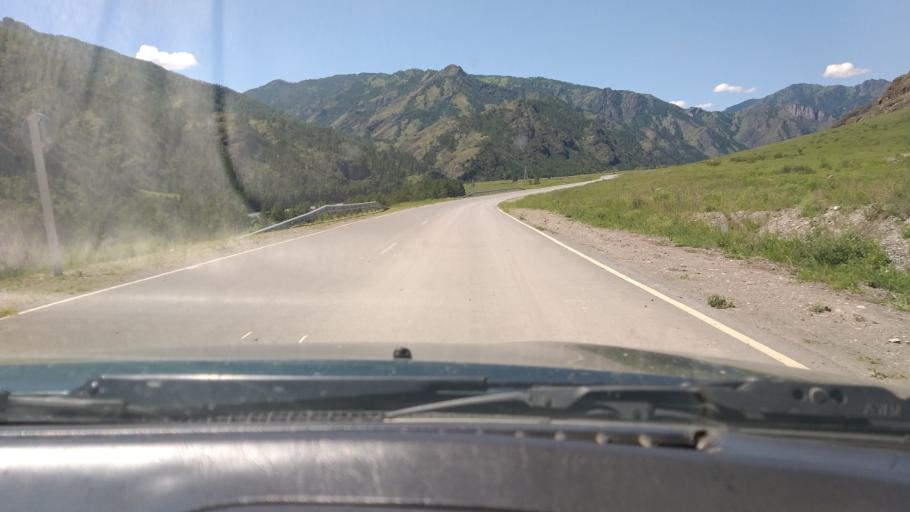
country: RU
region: Altay
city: Chemal
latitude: 51.1636
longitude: 86.1384
